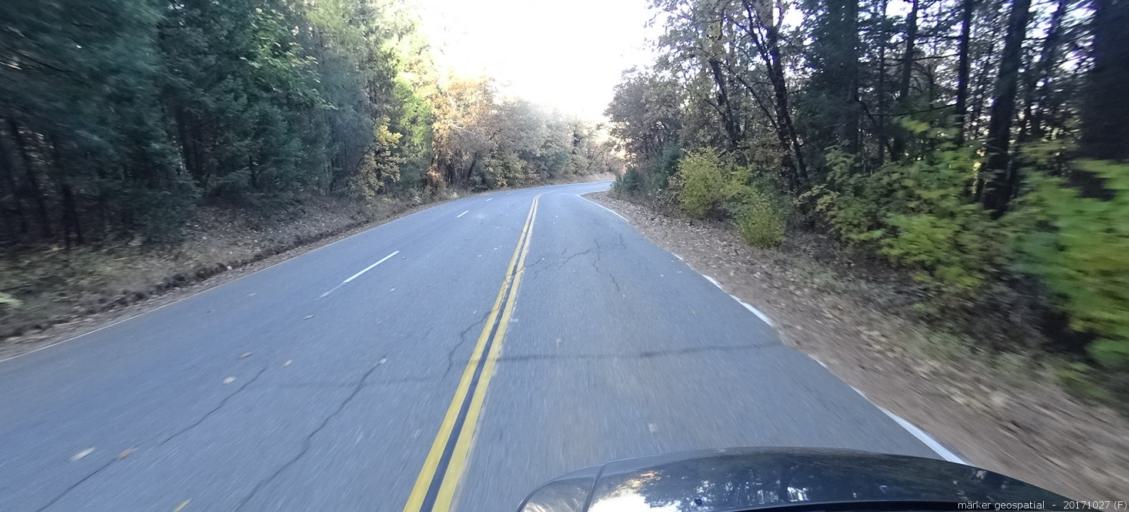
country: US
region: California
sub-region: Shasta County
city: Burney
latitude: 41.0046
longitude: -121.9133
